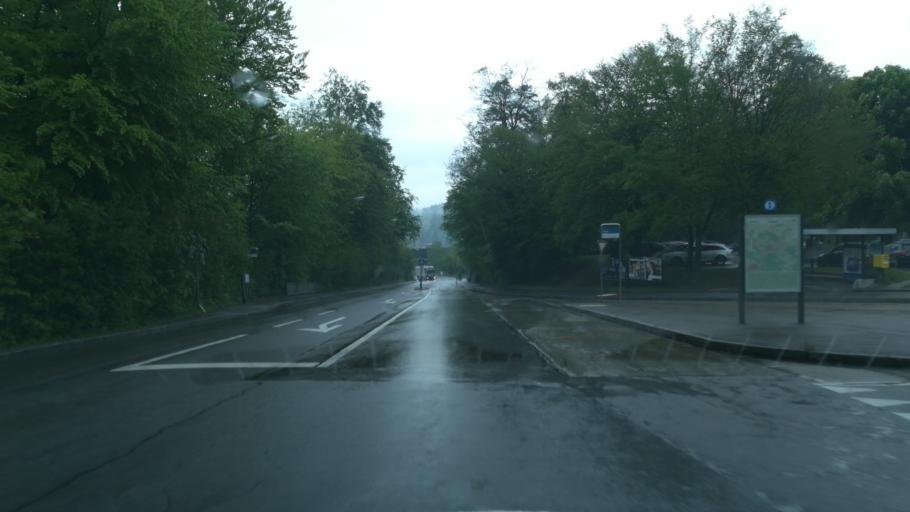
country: CH
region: Zurich
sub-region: Bezirk Winterthur
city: Toss
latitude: 47.4750
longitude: 8.7008
